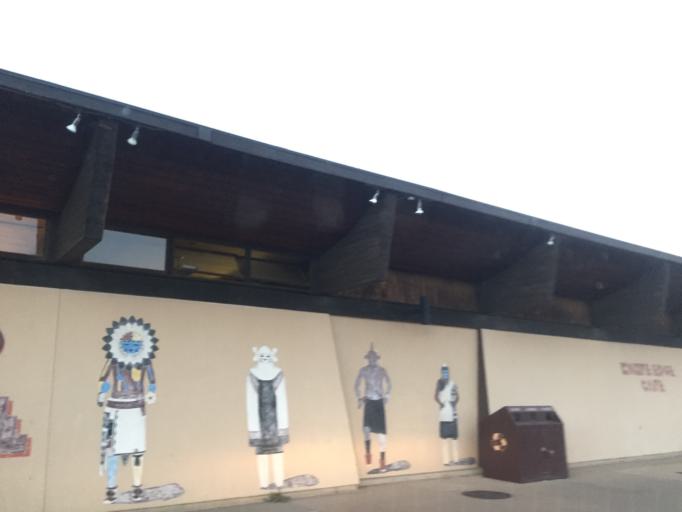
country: US
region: Colorado
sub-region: Montezuma County
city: Mancos
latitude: 37.2980
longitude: -108.4154
